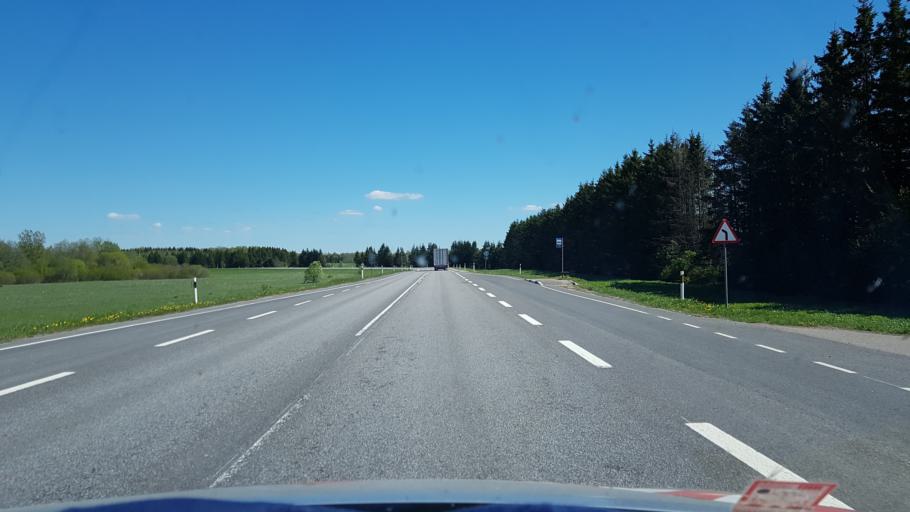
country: EE
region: Ida-Virumaa
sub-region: Narva-Joesuu linn
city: Narva-Joesuu
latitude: 59.3748
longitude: 27.9428
